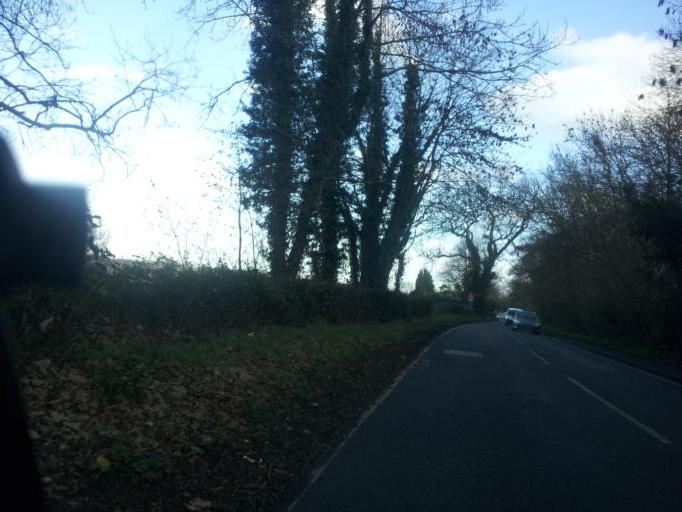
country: GB
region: England
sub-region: Kent
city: Meopham
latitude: 51.3774
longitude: 0.3651
